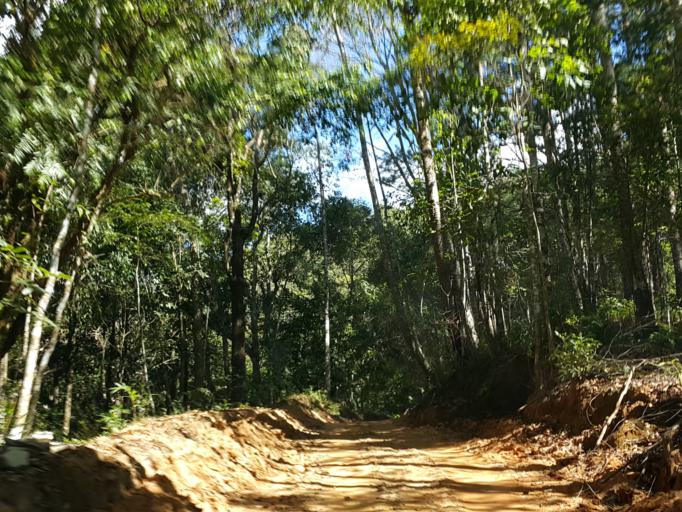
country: TH
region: Chiang Mai
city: Wiang Haeng
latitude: 19.5290
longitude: 98.8099
